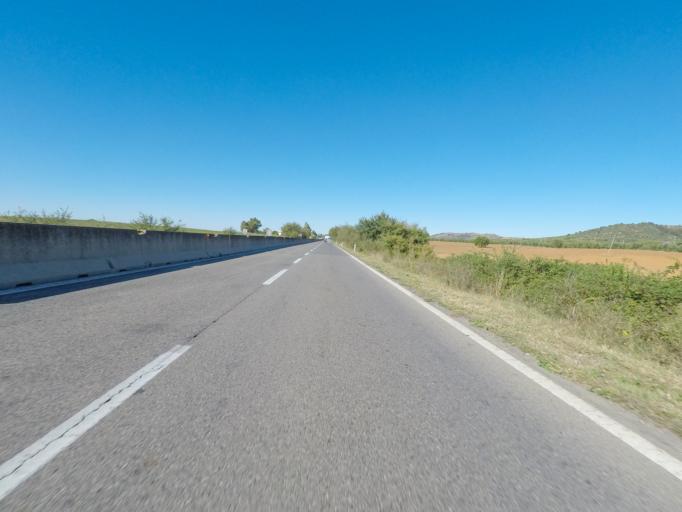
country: IT
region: Tuscany
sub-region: Provincia di Grosseto
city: Grosseto
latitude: 42.6935
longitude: 11.1381
